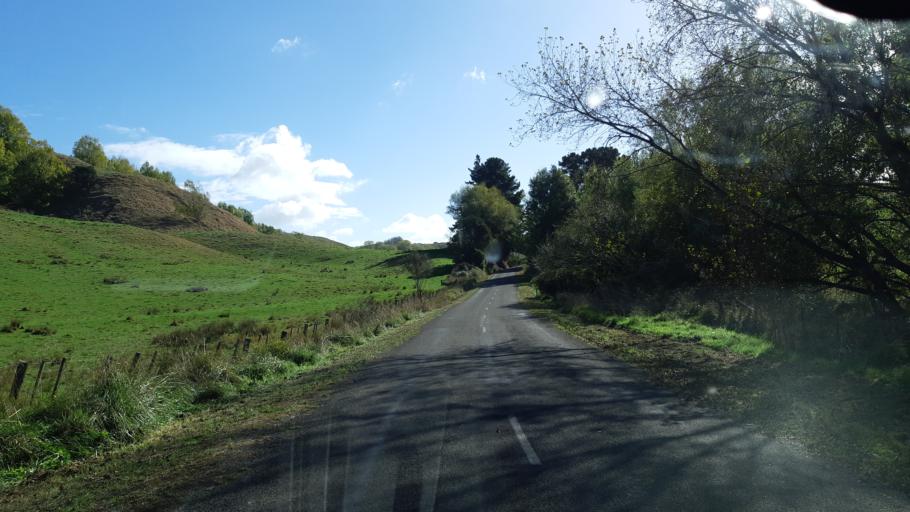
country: NZ
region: Manawatu-Wanganui
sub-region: Wanganui District
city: Wanganui
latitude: -39.8978
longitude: 175.3180
